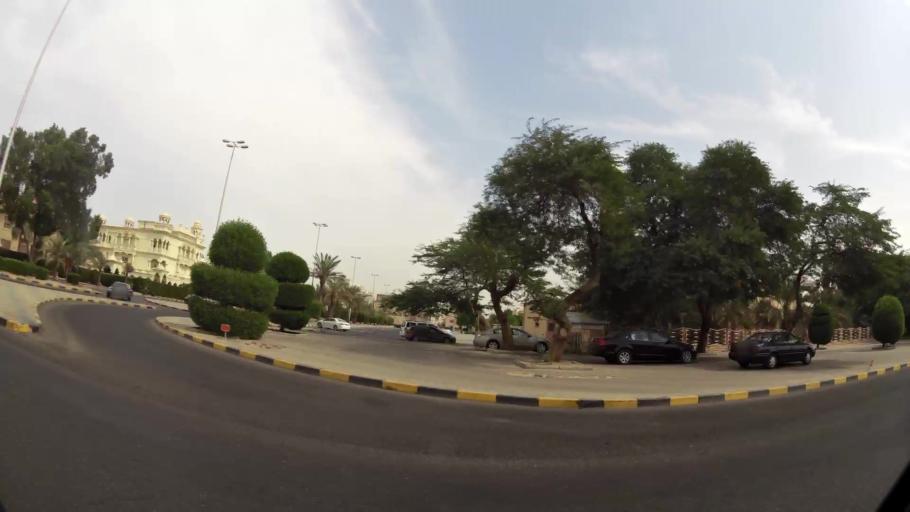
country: KW
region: Al Asimah
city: Ash Shamiyah
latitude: 29.3320
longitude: 47.9888
